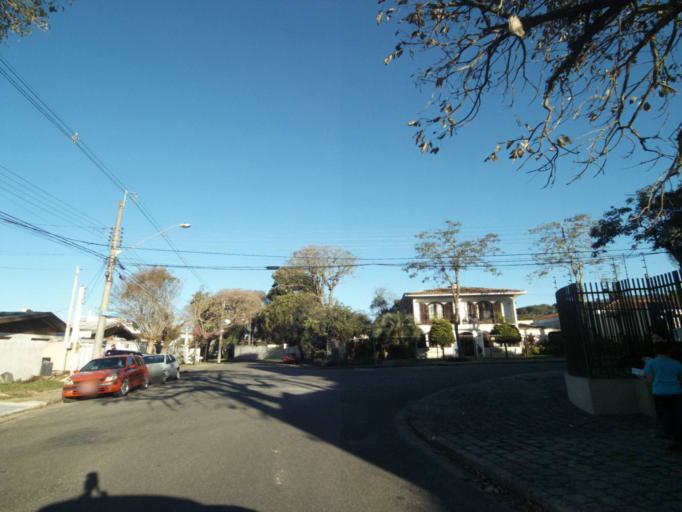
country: BR
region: Parana
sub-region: Pinhais
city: Pinhais
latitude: -25.4190
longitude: -49.2279
